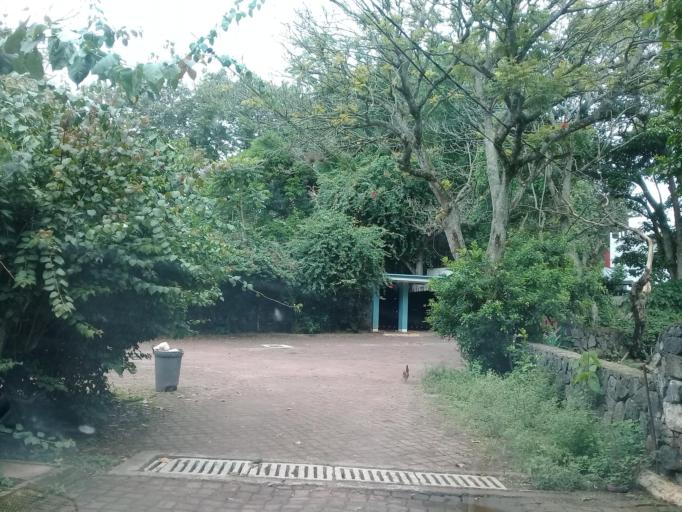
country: MX
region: Veracruz
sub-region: Xalapa
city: Colonia Santa Barbara
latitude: 19.5256
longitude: -96.8766
